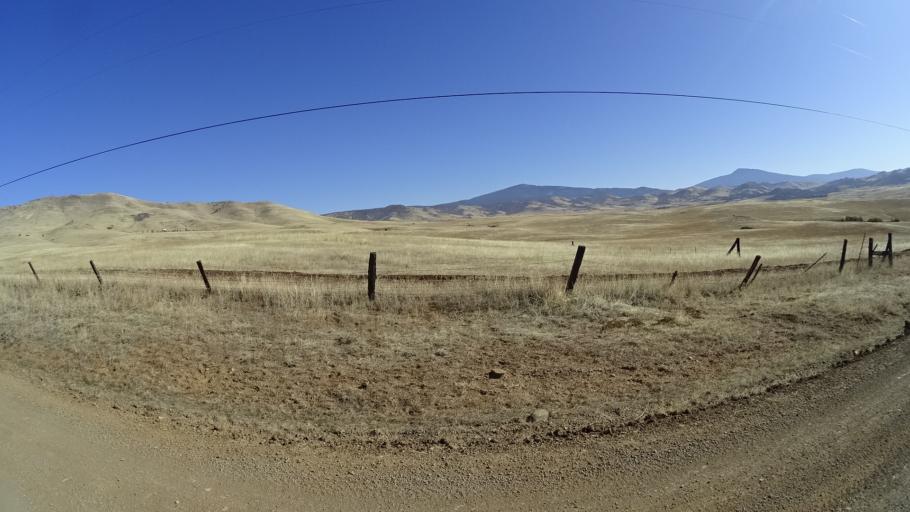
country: US
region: California
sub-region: Siskiyou County
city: Montague
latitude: 41.8372
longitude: -122.4206
